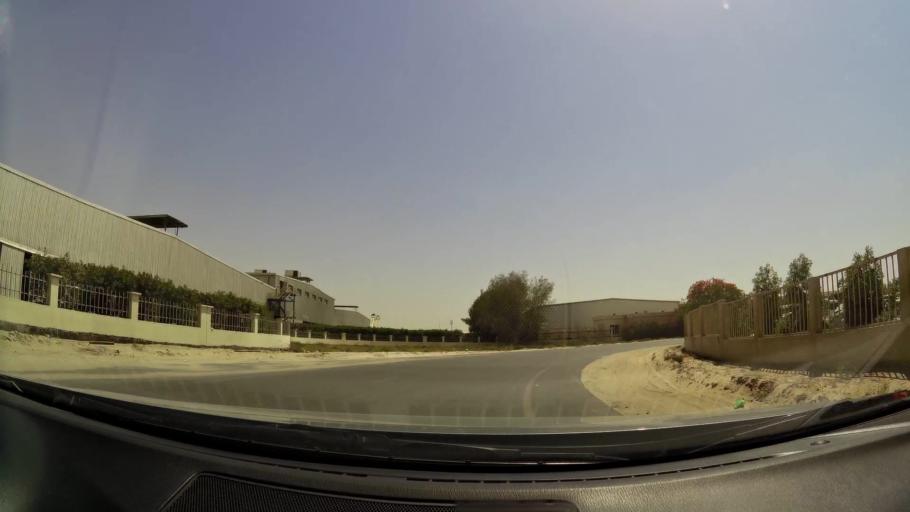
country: AE
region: Dubai
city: Dubai
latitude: 24.9854
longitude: 55.1592
